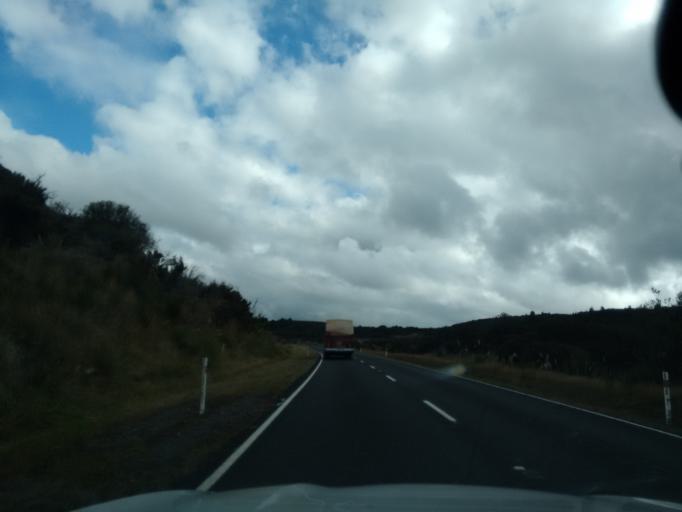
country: NZ
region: Waikato
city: Turangi
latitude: -39.0533
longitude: 175.5882
